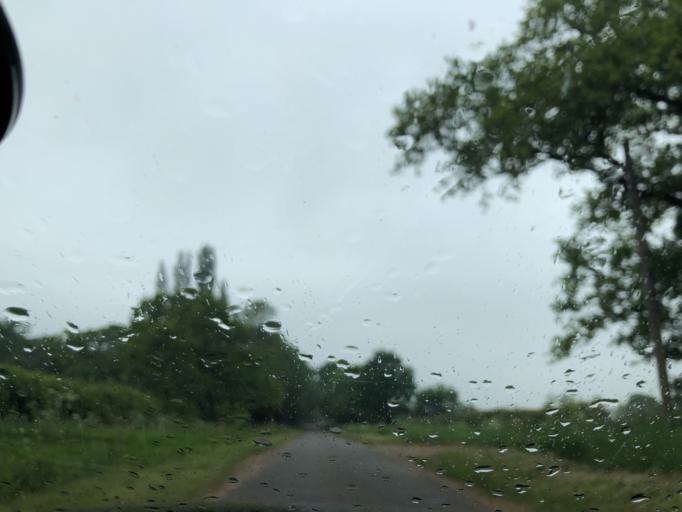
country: GB
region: England
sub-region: Warwickshire
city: Wroxall
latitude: 52.3482
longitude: -1.6473
